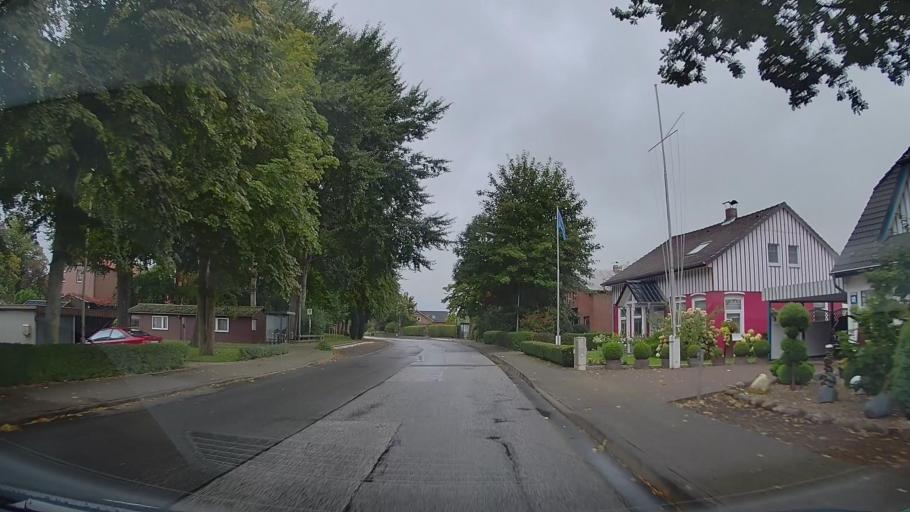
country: DE
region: Schleswig-Holstein
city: Brokdorf
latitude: 53.8614
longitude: 9.3311
